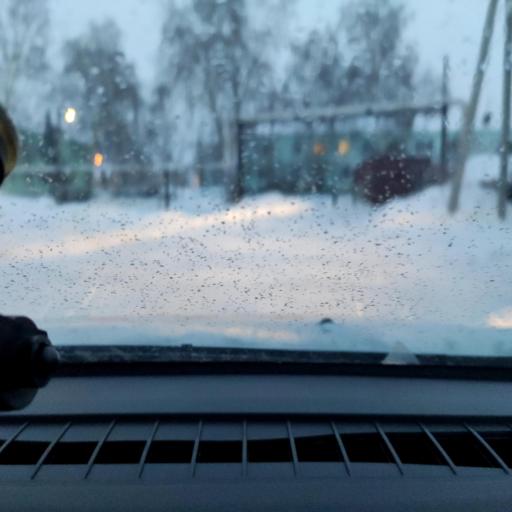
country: RU
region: Samara
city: Kinel'-Cherkassy
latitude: 53.4665
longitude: 51.5157
